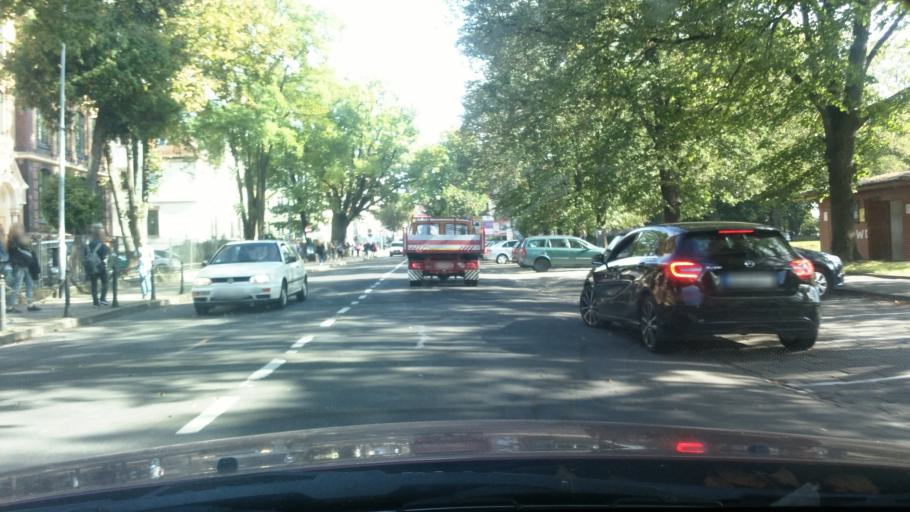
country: PL
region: Lower Silesian Voivodeship
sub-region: Powiat zgorzelecki
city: Zgorzelec
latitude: 51.1487
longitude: 15.0042
